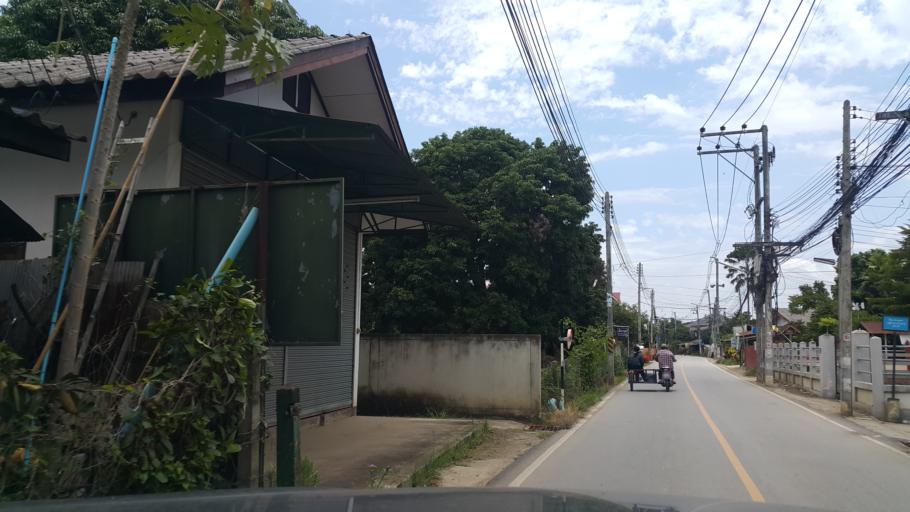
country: TH
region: Chiang Mai
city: Saraphi
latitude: 18.7228
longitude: 98.9886
